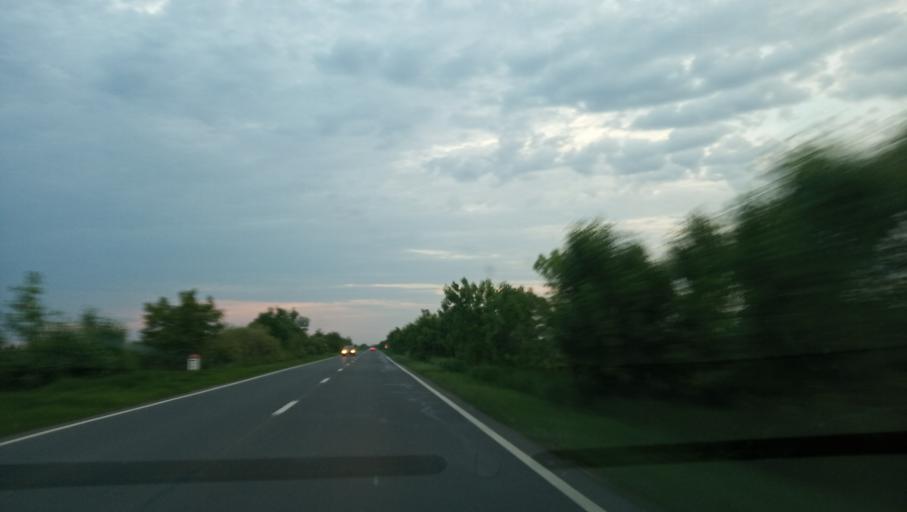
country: RO
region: Timis
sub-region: Comuna Padureni
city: Padureni
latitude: 45.5908
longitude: 21.1999
